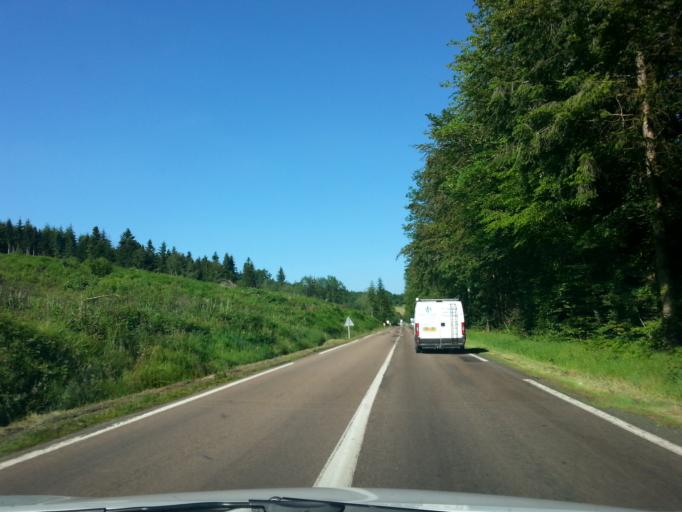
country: FR
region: Rhone-Alpes
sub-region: Departement de la Loire
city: Belmont-de-la-Loire
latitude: 46.1613
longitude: 4.4584
